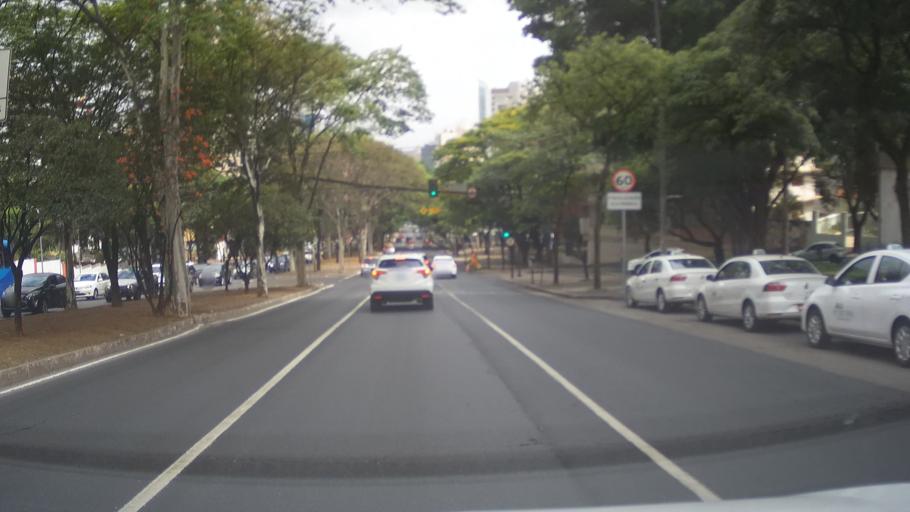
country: BR
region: Minas Gerais
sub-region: Belo Horizonte
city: Belo Horizonte
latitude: -19.9383
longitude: -43.9266
